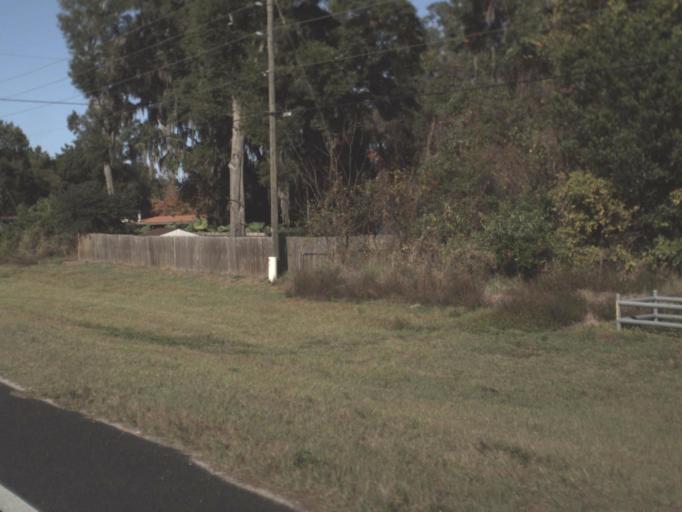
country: US
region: Florida
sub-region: Marion County
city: Belleview
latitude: 29.0261
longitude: -82.0902
